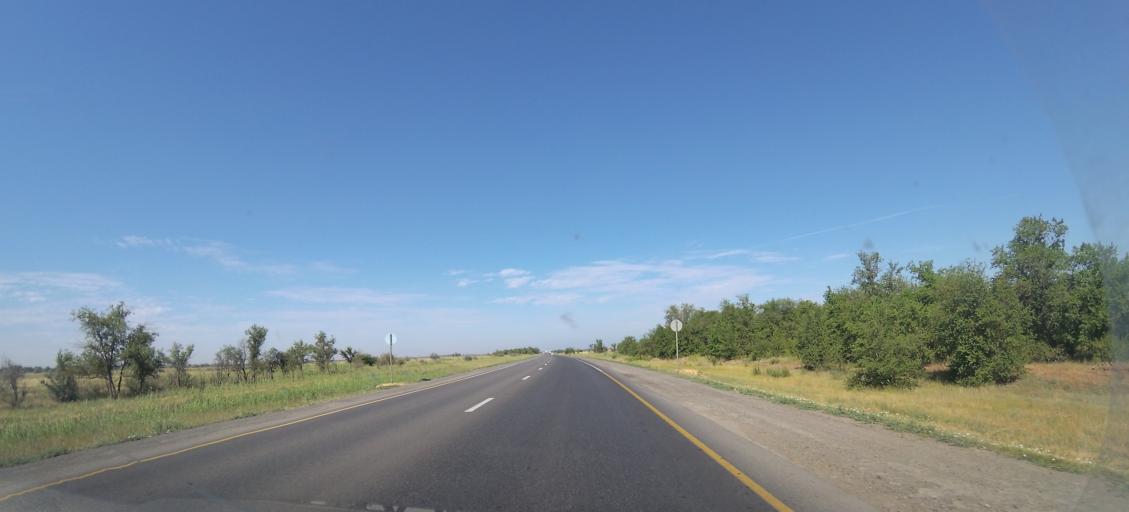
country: RU
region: Volgograd
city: Bereslavka
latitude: 48.6855
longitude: 43.9388
